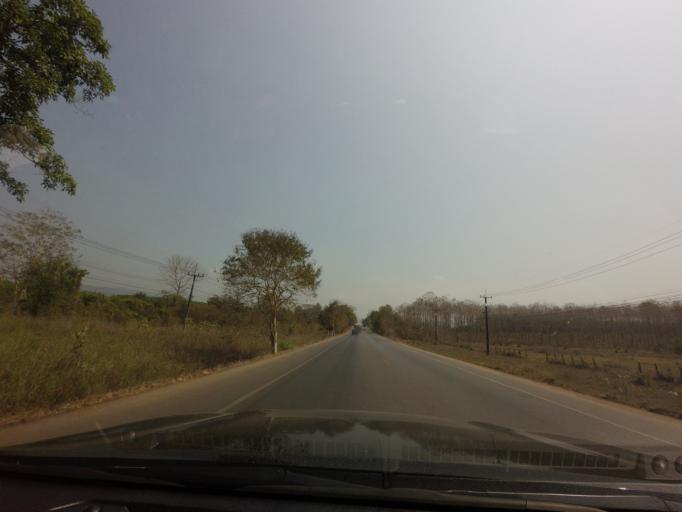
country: TH
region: Kanchanaburi
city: Thong Pha Phum
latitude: 14.6421
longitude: 98.6917
